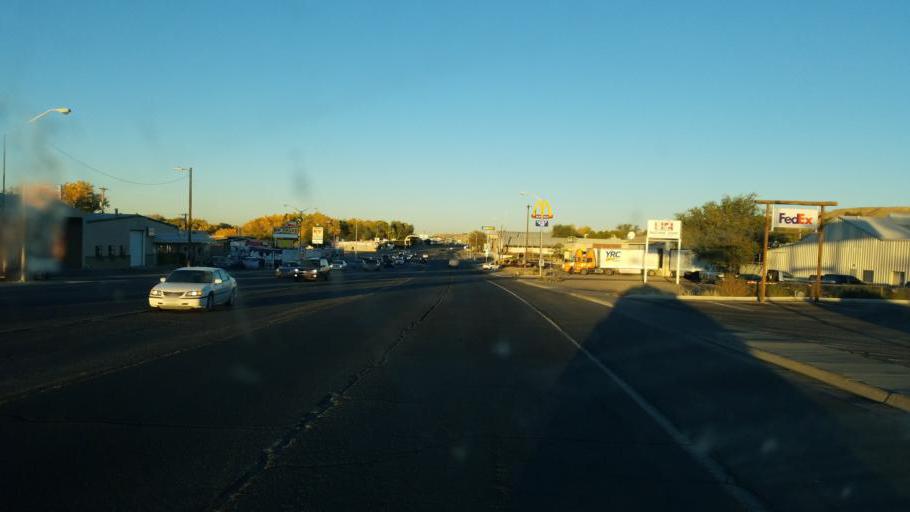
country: US
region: New Mexico
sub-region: San Juan County
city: Farmington
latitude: 36.7315
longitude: -108.2297
